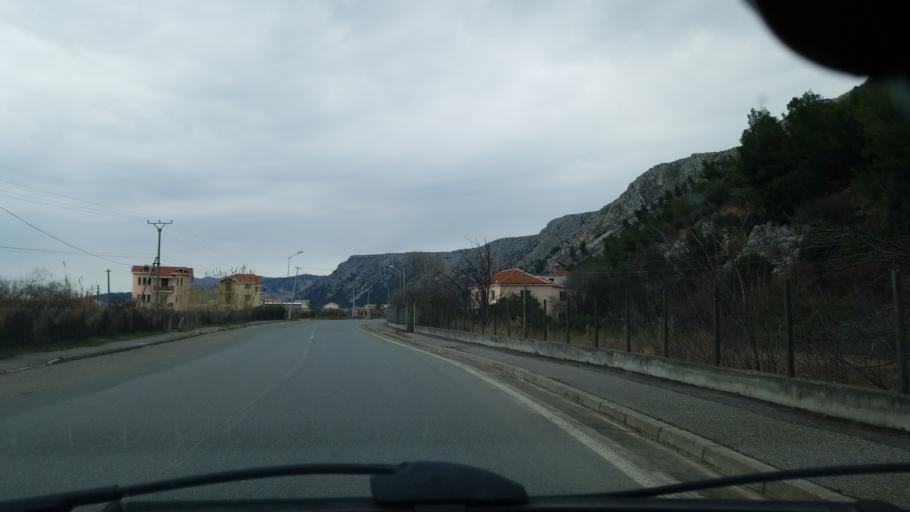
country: AL
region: Lezhe
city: Lezhe
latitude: 41.7929
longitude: 19.6225
